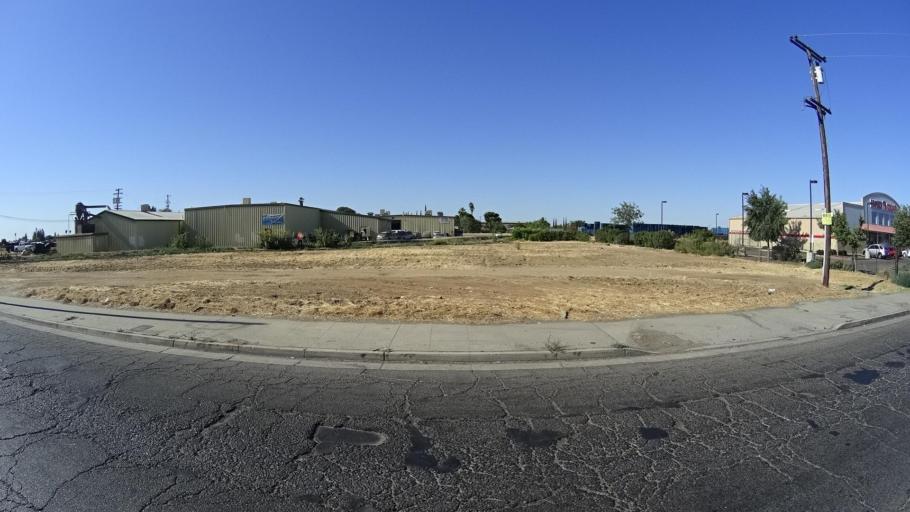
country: US
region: California
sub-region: Fresno County
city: Fresno
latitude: 36.7069
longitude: -119.7888
